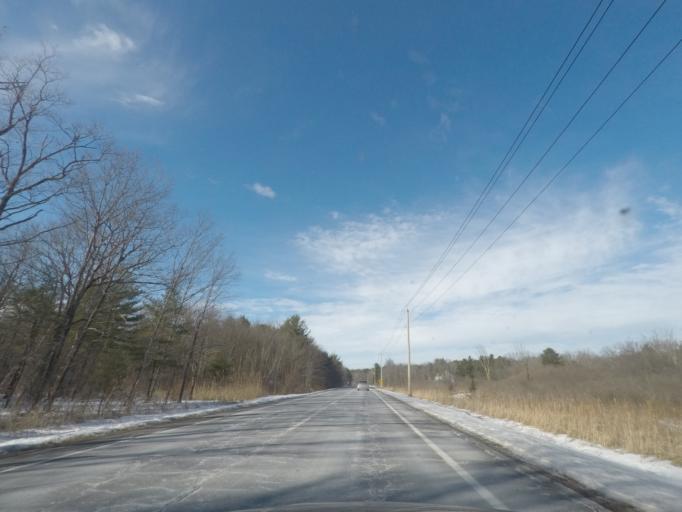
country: US
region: New York
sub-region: Albany County
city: Altamont
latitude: 42.7027
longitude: -73.9743
